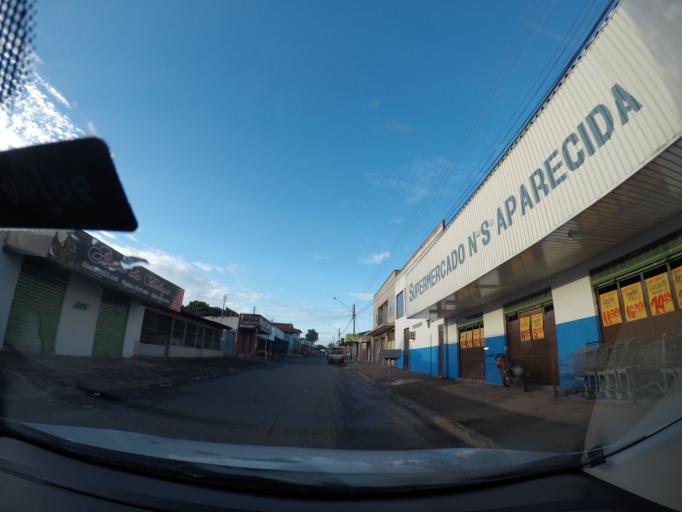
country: BR
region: Goias
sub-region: Goiania
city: Goiania
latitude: -16.6985
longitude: -49.3519
